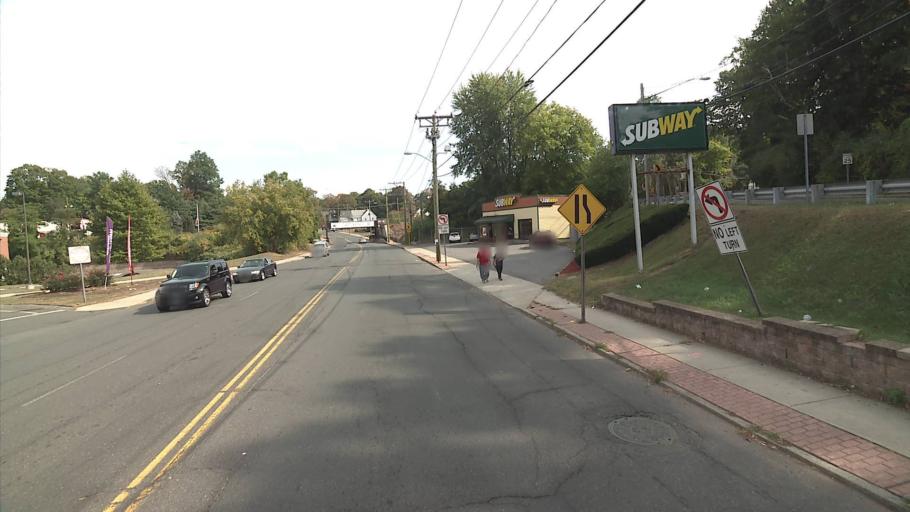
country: US
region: Connecticut
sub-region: Hartford County
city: Manchester
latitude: 41.7727
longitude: -72.5321
